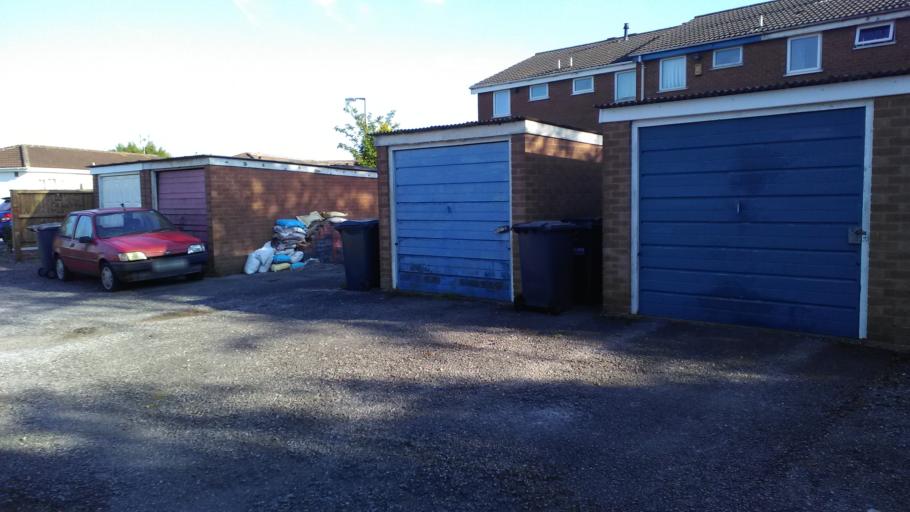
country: GB
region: England
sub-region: Nottinghamshire
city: Arnold
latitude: 52.9963
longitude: -1.1023
